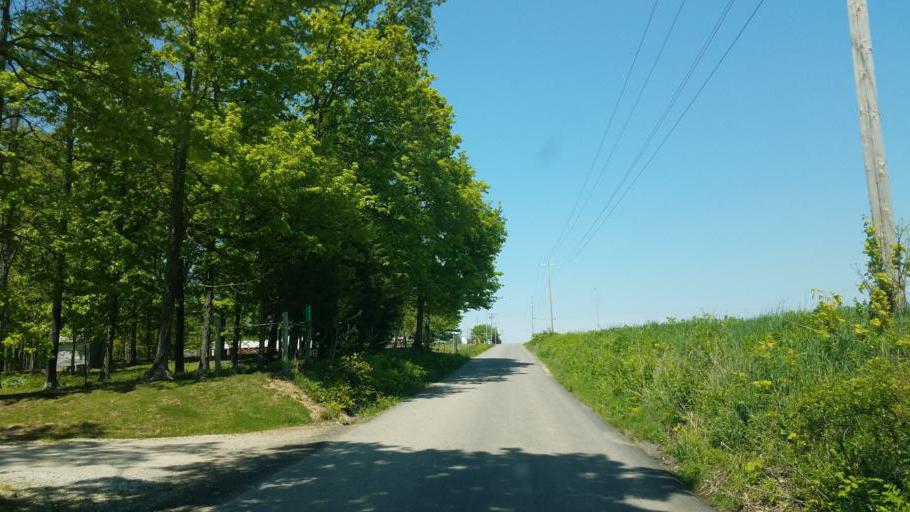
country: US
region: Ohio
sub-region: Knox County
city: Fredericktown
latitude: 40.5558
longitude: -82.6238
